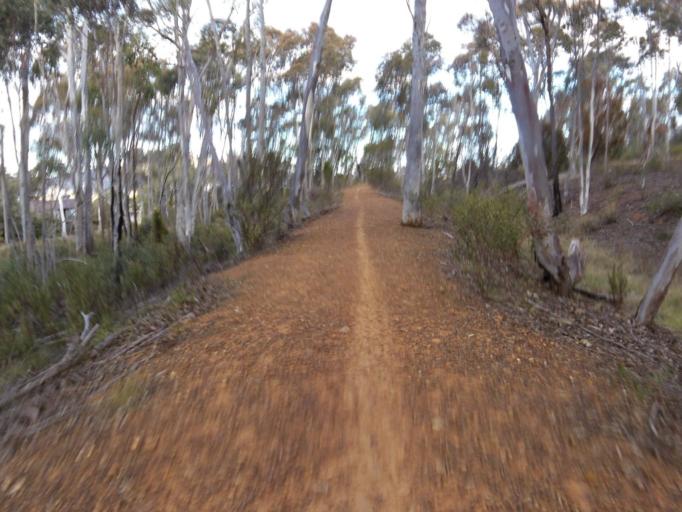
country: AU
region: Australian Capital Territory
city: Acton
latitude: -35.2616
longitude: 149.1111
